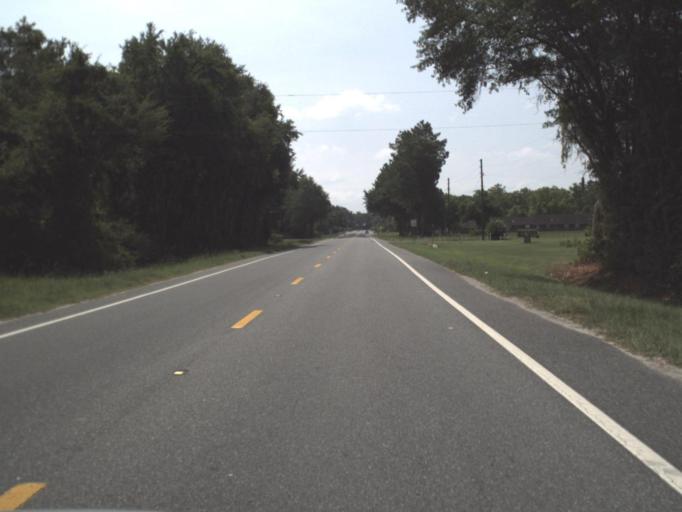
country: US
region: Georgia
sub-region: Echols County
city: Statenville
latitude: 30.6081
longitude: -83.1051
